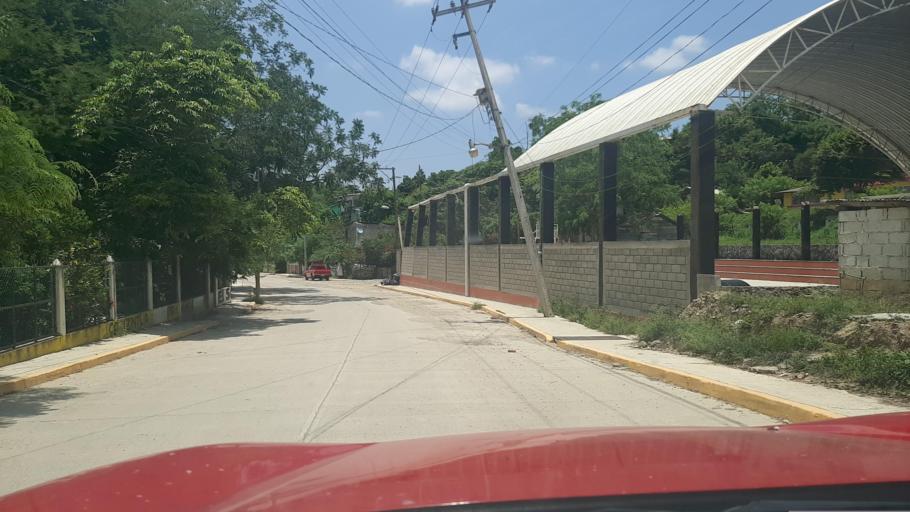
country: MX
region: Veracruz
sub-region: Poza Rica de Hidalgo
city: Arroyo del Maiz Uno
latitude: 20.4974
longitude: -97.4232
